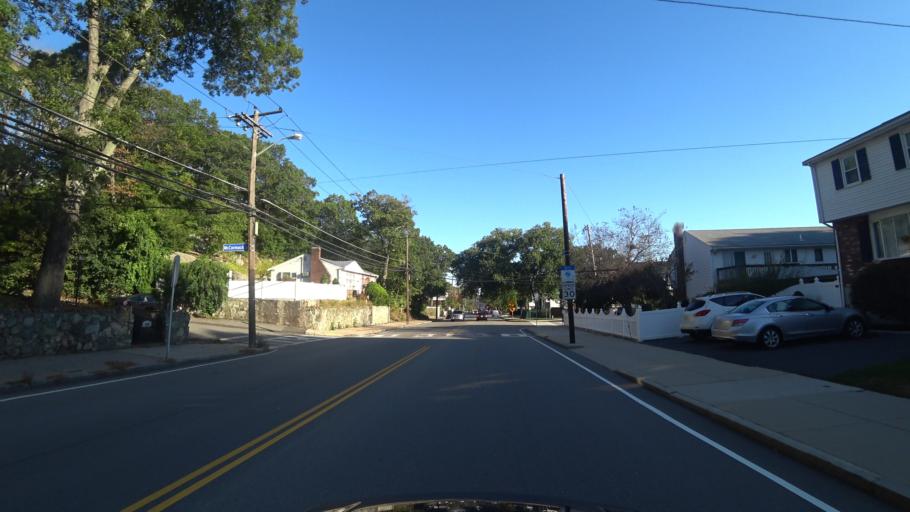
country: US
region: Massachusetts
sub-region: Middlesex County
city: Malden
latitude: 42.4358
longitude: -71.0856
